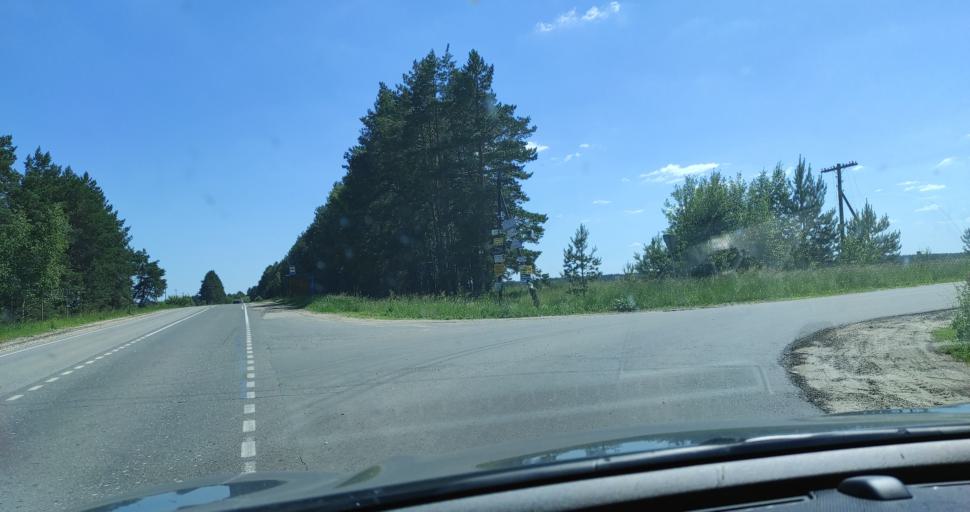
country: RU
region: Rjazan
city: Murmino
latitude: 54.5732
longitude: 40.1124
